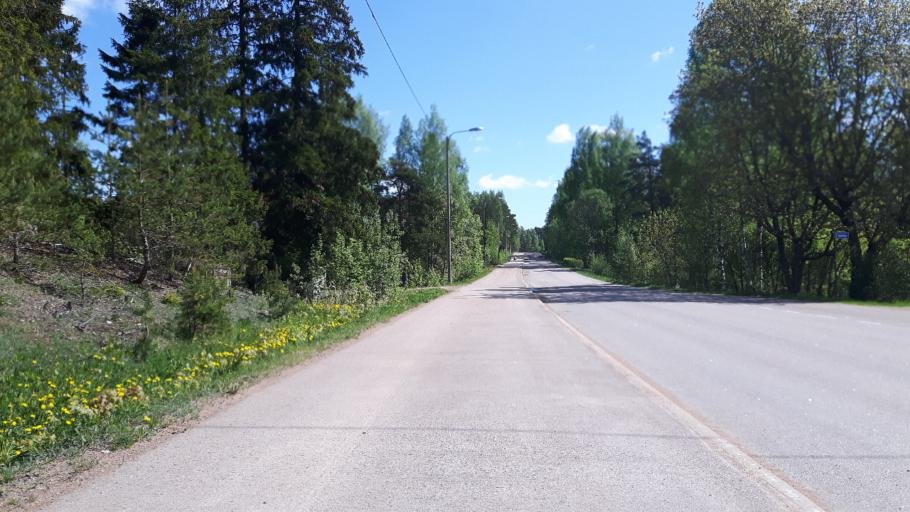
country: FI
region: Kymenlaakso
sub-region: Kotka-Hamina
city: Virolahti
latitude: 60.5160
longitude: 27.4506
